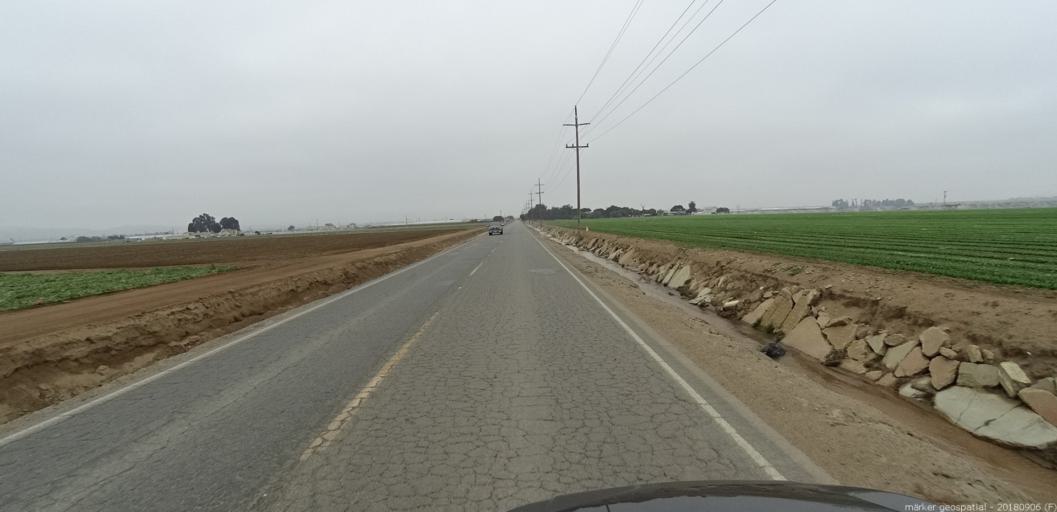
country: US
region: California
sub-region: Monterey County
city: Chualar
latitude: 36.6354
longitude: -121.5557
